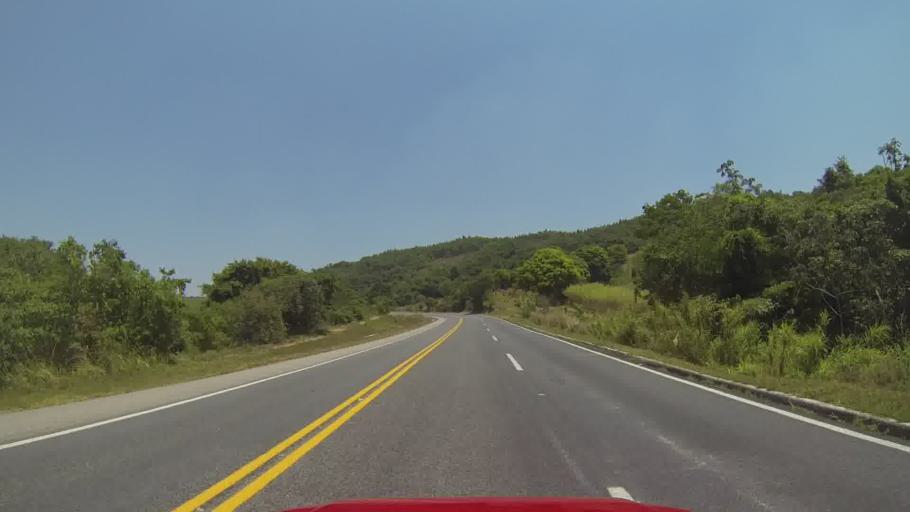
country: BR
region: Minas Gerais
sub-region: Itapecerica
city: Itapecerica
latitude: -20.2886
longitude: -45.1530
